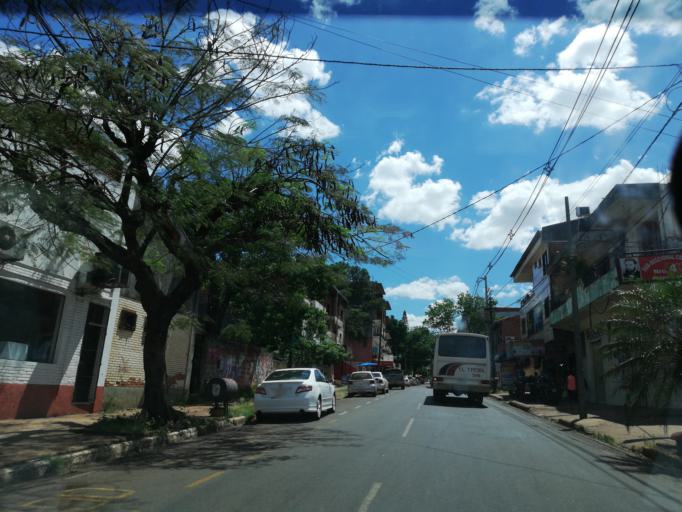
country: PY
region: Itapua
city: Encarnacion
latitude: -27.3404
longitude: -55.8581
